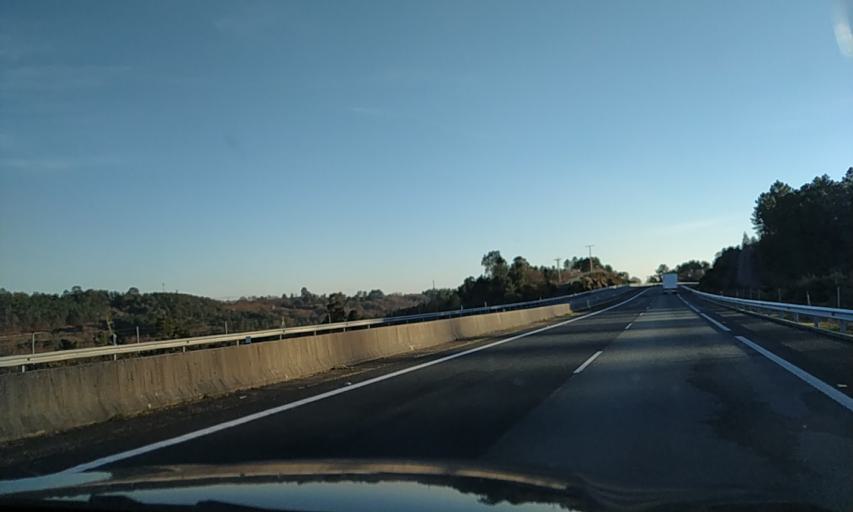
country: ES
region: Galicia
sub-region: Provincia de Ourense
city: Pinor
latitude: 42.5086
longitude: -8.0226
